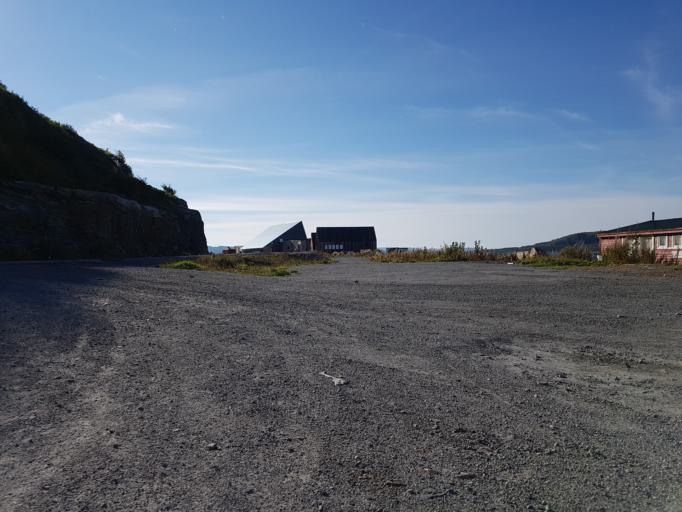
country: NO
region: Sor-Trondelag
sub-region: Afjord
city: A i Afjord
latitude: 64.0479
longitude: 9.9453
